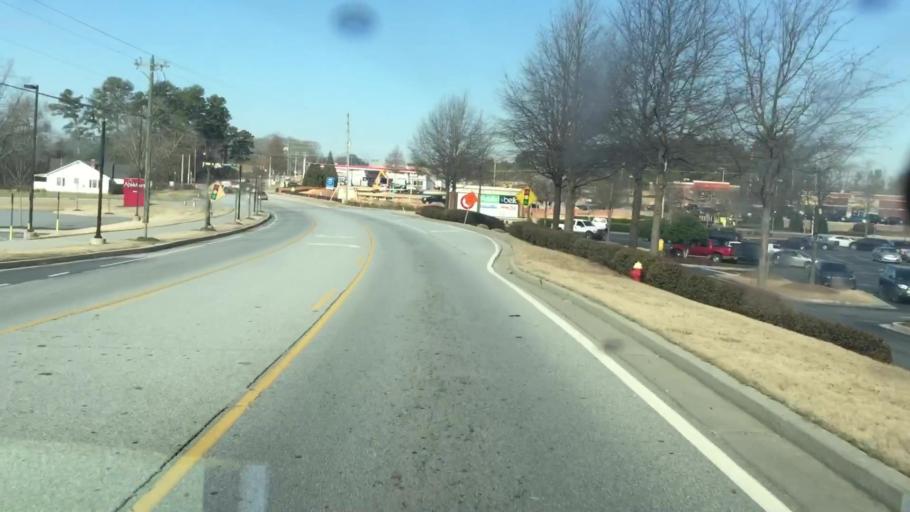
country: US
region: Georgia
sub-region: Barrow County
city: Winder
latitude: 33.9427
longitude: -83.7549
